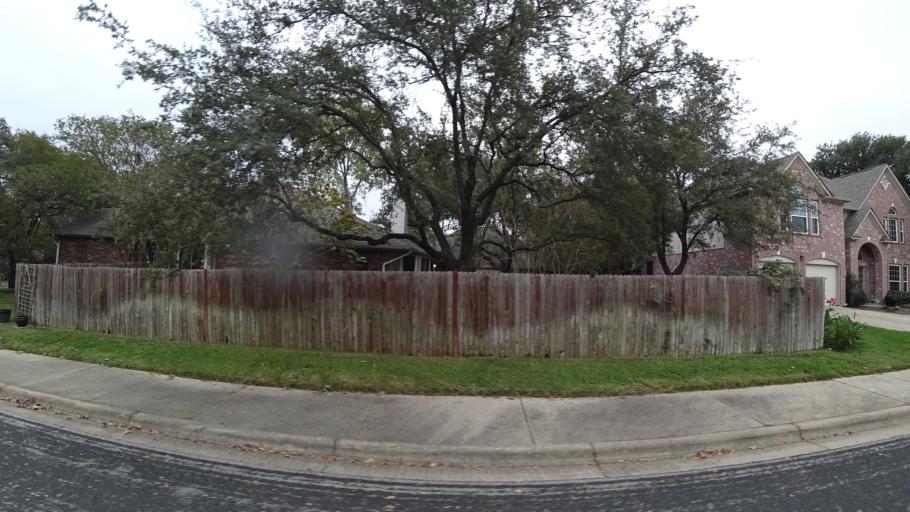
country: US
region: Texas
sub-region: Williamson County
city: Anderson Mill
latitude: 30.4353
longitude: -97.8194
